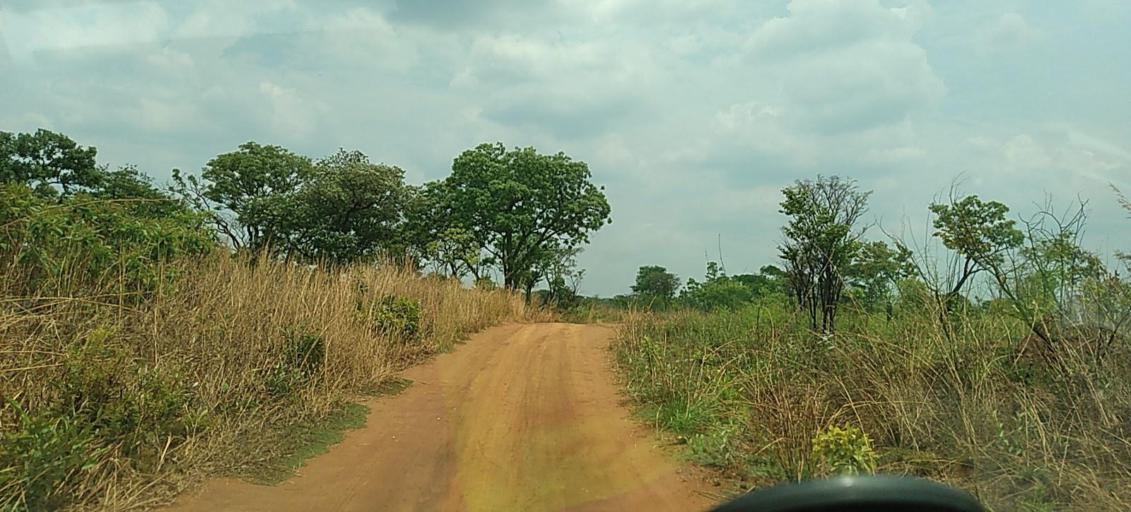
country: ZM
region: North-Western
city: Kansanshi
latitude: -12.0483
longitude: 26.3674
